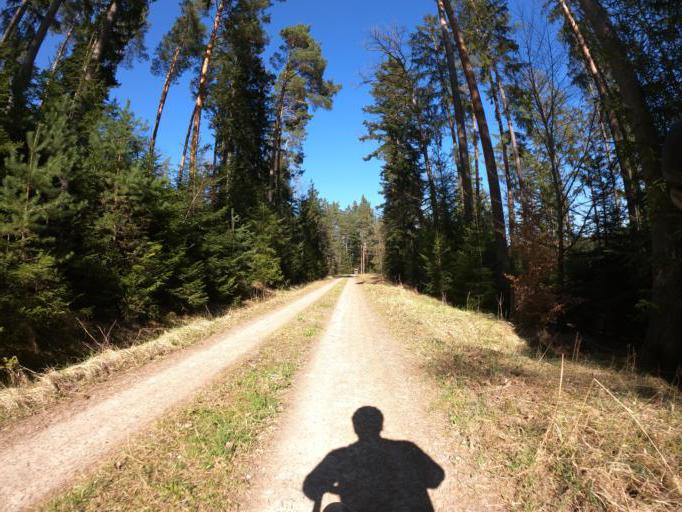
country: DE
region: Baden-Wuerttemberg
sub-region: Tuebingen Region
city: Hirrlingen
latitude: 48.4003
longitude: 8.9293
